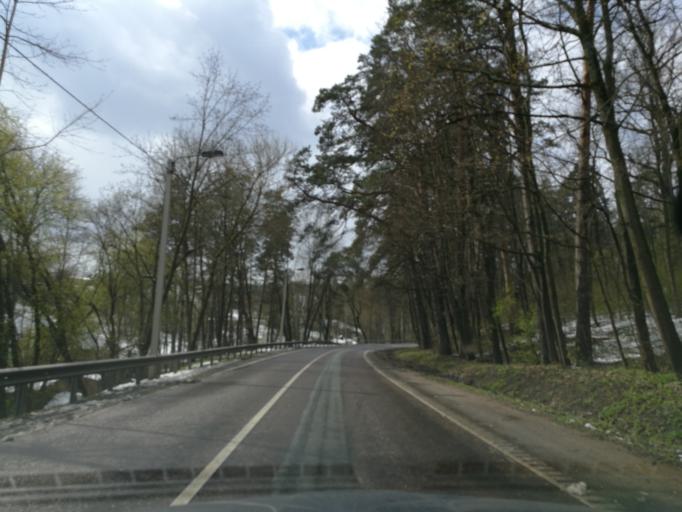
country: LT
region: Kauno apskritis
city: Dainava (Kaunas)
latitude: 54.8669
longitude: 23.9858
